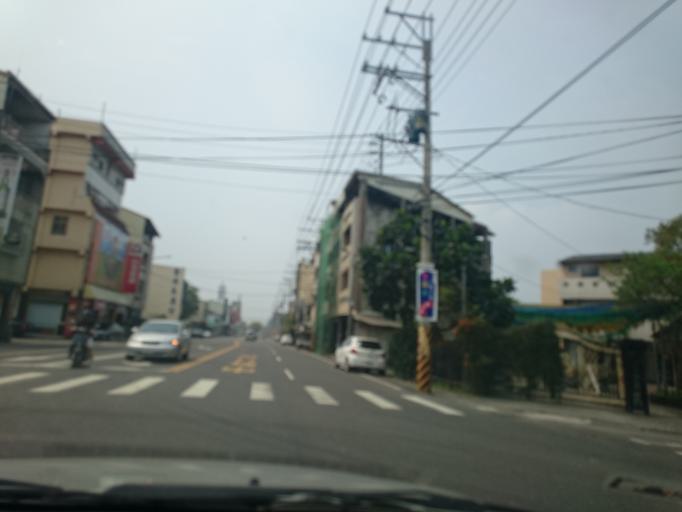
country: TW
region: Taiwan
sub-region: Nantou
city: Nantou
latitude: 23.8745
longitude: 120.5157
